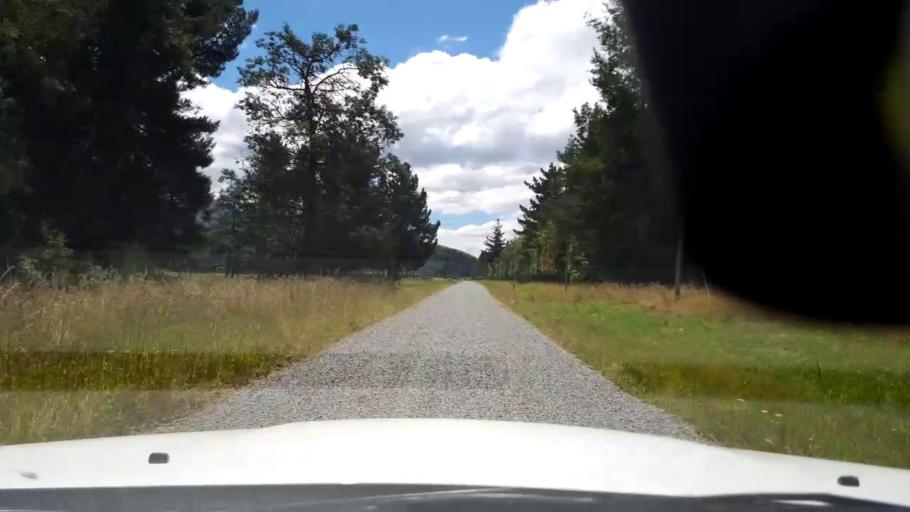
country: NZ
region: Canterbury
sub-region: Timaru District
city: Pleasant Point
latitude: -43.9670
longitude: 171.2262
